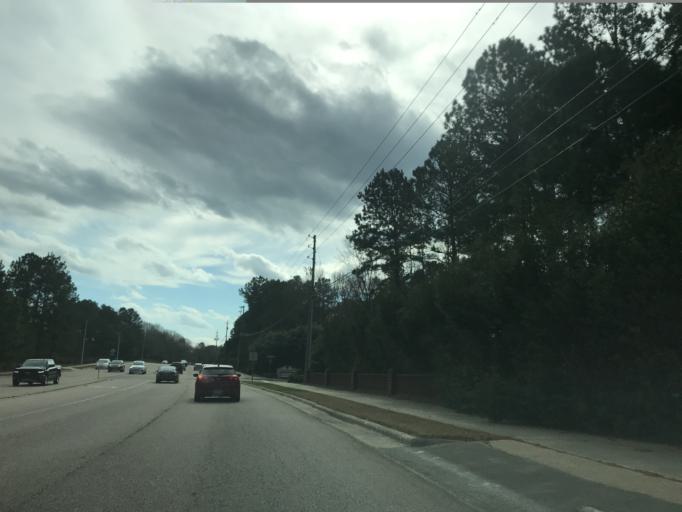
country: US
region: North Carolina
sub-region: Wake County
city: Morrisville
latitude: 35.8118
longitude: -78.8483
